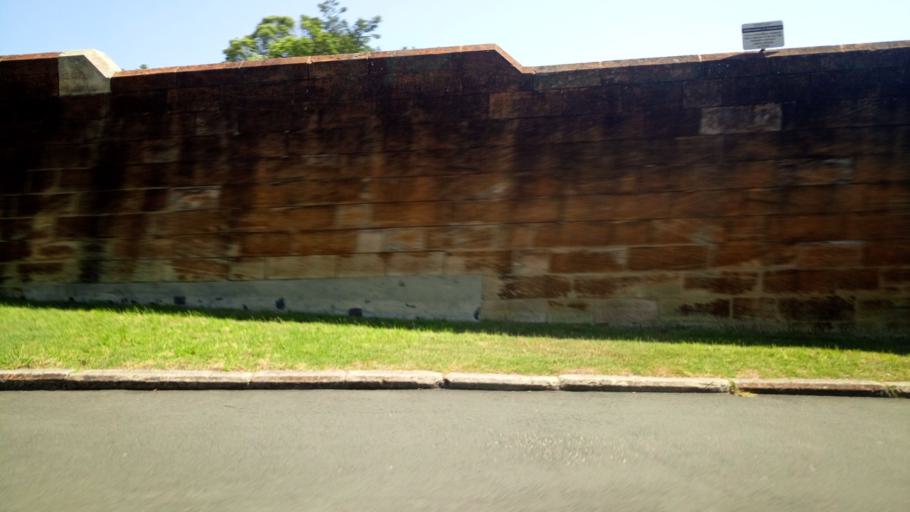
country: AU
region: New South Wales
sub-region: Woollahra
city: Paddington
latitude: -33.8848
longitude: 151.2249
